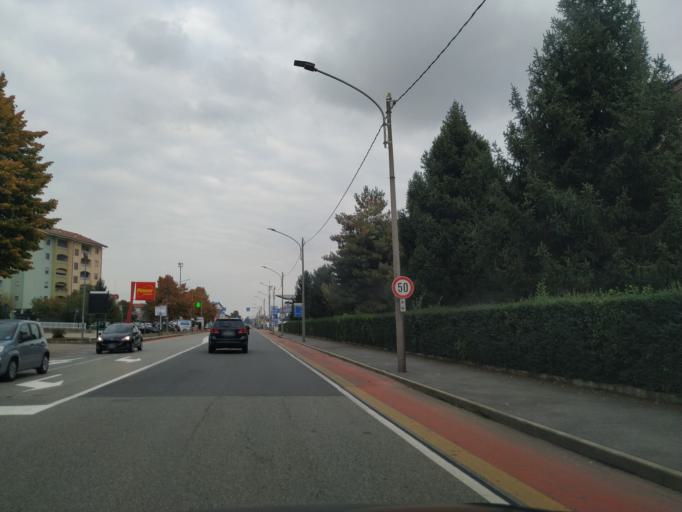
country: IT
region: Piedmont
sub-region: Provincia di Torino
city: Chivasso
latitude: 45.1941
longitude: 7.9087
